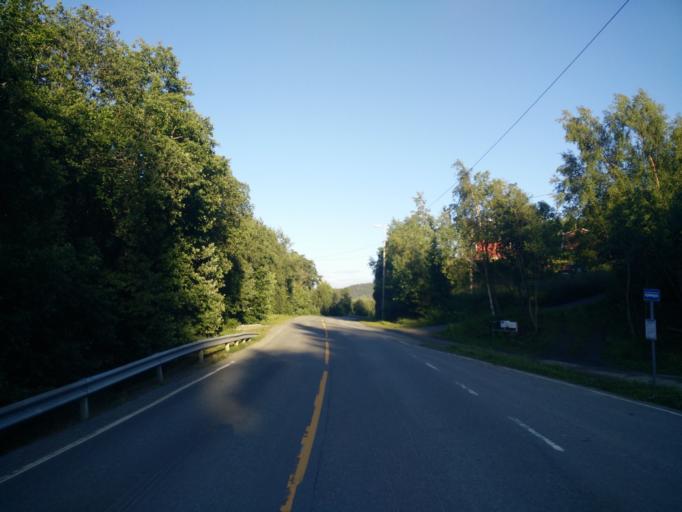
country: NO
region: Sor-Trondelag
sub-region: Skaun
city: Borsa
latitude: 63.3427
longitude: 10.0543
